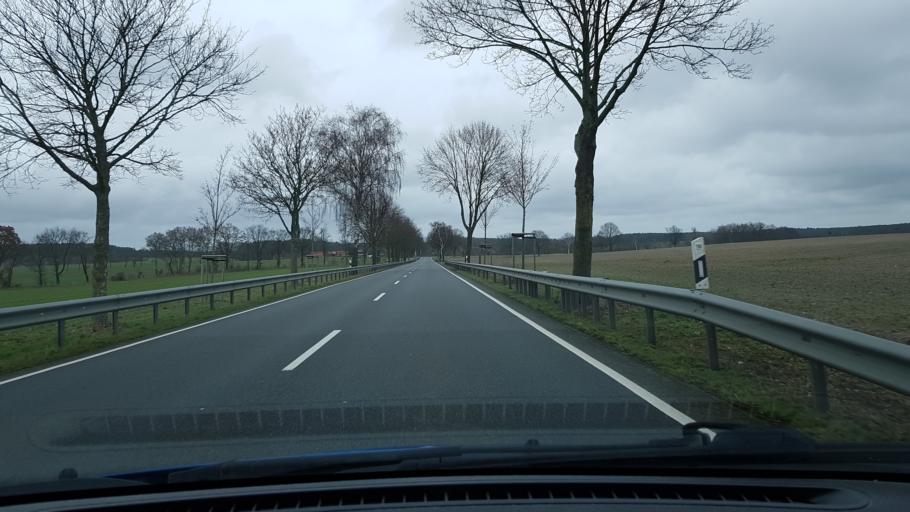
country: DE
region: Lower Saxony
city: Rosche
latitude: 53.0207
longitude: 10.7451
